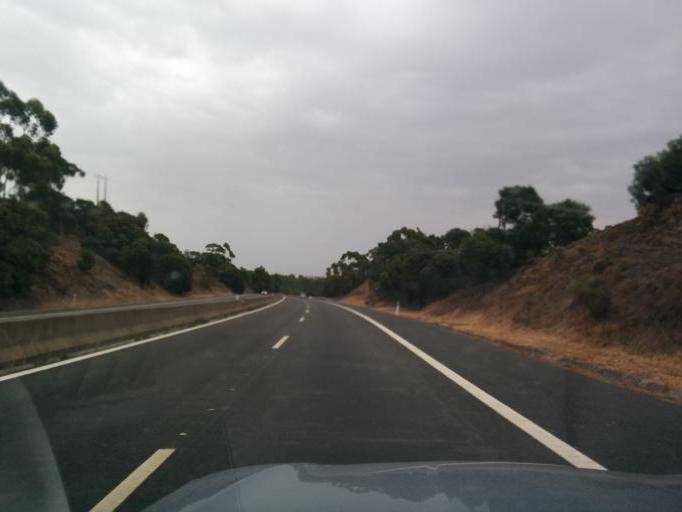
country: PT
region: Faro
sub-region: Tavira
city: Tavira
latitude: 37.1770
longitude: -7.5988
